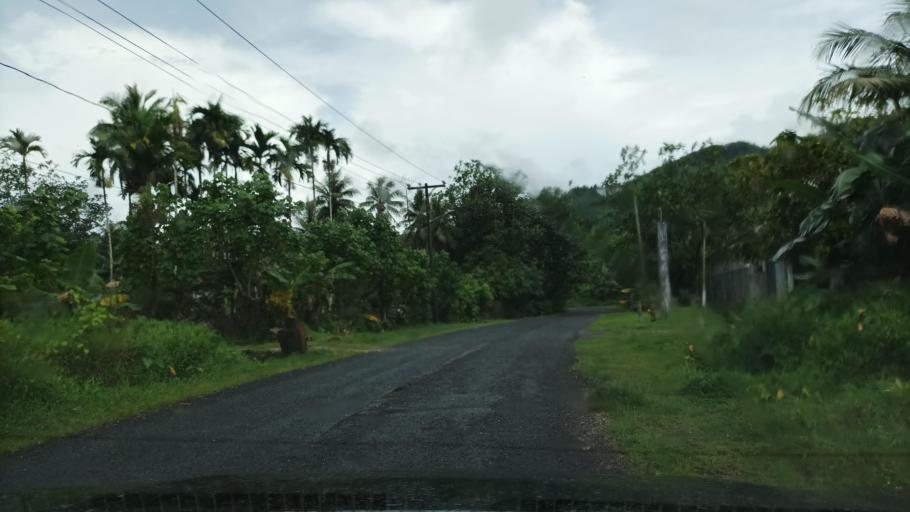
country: FM
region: Pohnpei
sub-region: Madolenihm Municipality
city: Madolenihm Municipality Government
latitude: 6.9144
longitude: 158.2927
